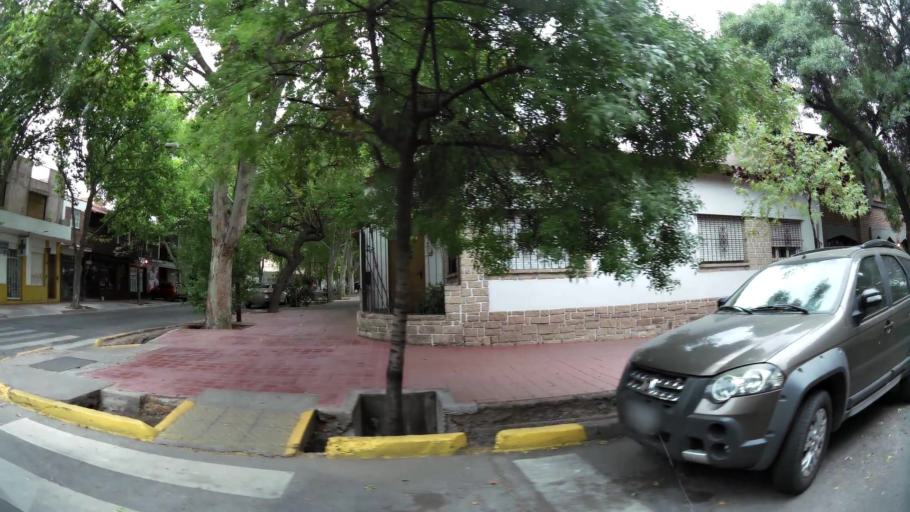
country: AR
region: Mendoza
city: Mendoza
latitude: -32.8906
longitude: -68.8522
